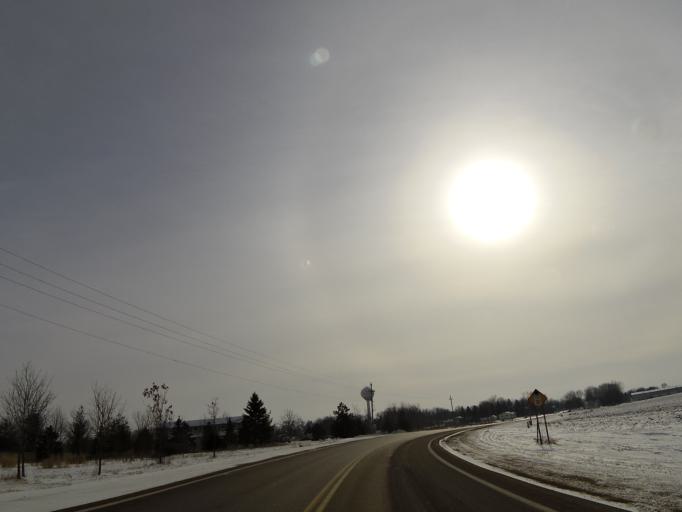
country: US
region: Minnesota
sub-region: McLeod County
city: Lester Prairie
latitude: 44.8911
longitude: -93.9707
